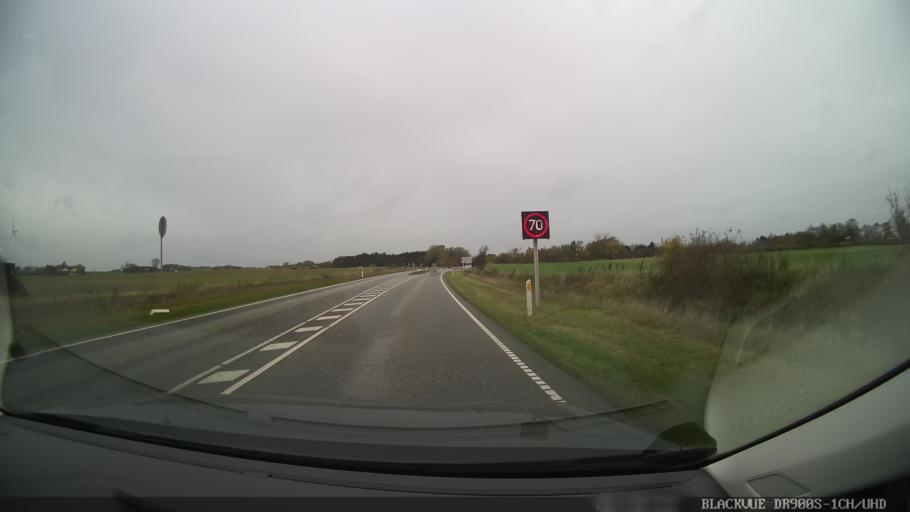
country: DK
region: North Denmark
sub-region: Thisted Kommune
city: Thisted
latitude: 56.8289
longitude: 8.7157
